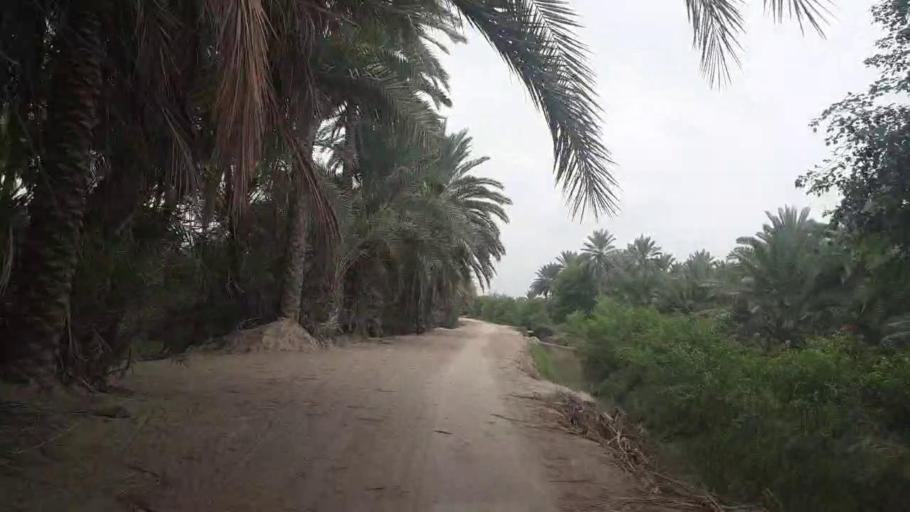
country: PK
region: Sindh
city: Khairpur
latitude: 27.5836
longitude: 68.7126
